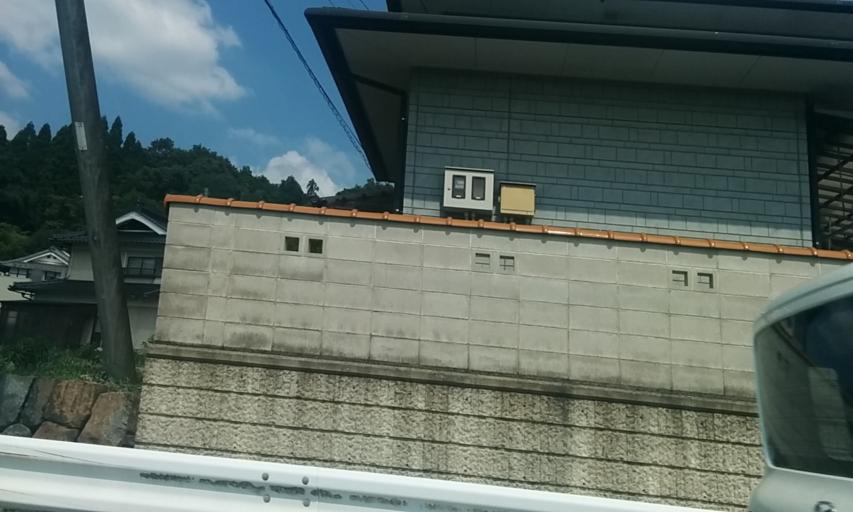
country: JP
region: Kyoto
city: Fukuchiyama
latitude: 35.3182
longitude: 135.1225
